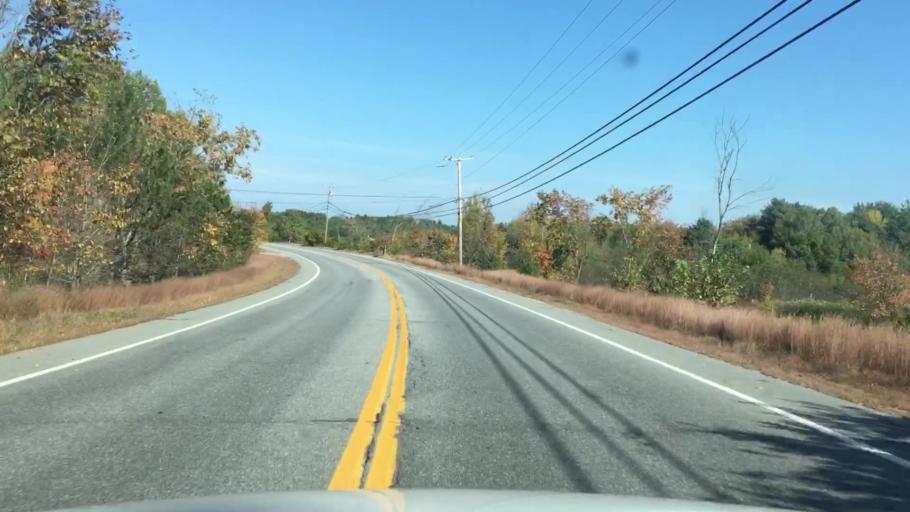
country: US
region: Maine
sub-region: Sagadahoc County
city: Topsham
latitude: 43.9702
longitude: -69.9578
